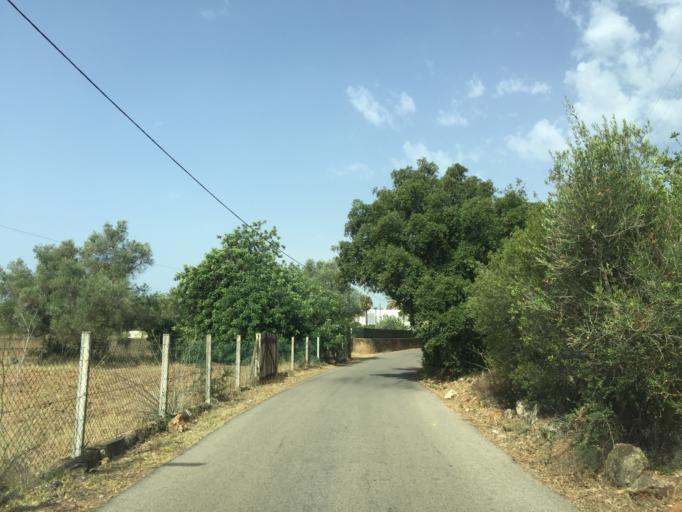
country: PT
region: Faro
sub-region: Loule
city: Vilamoura
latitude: 37.1052
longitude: -8.1045
